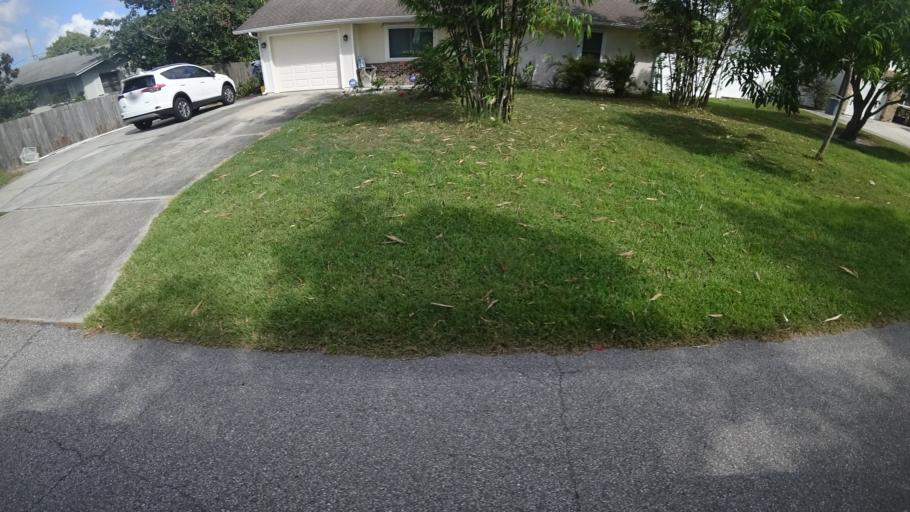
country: US
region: Florida
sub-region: Manatee County
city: Memphis
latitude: 27.5554
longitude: -82.5669
